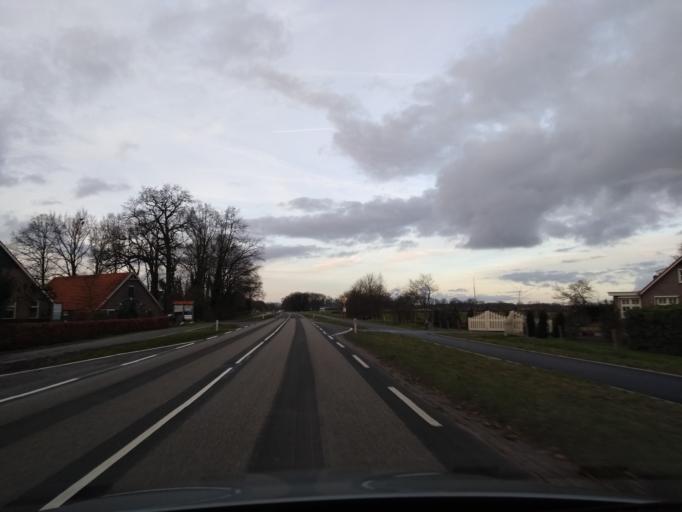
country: NL
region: Overijssel
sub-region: Gemeente Oldenzaal
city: Oldenzaal
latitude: 52.3133
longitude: 6.8608
